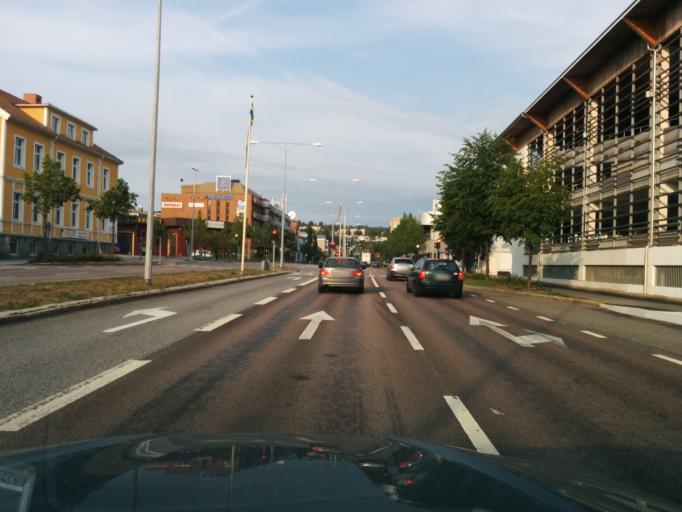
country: SE
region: Vaesternorrland
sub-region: OErnskoeldsviks Kommun
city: Ornskoldsvik
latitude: 63.2909
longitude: 18.7112
